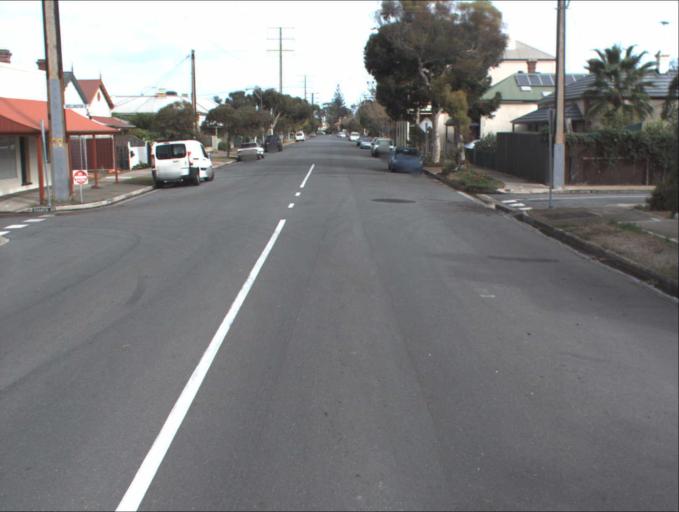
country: AU
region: South Australia
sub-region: Port Adelaide Enfield
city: Birkenhead
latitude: -34.8380
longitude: 138.4926
